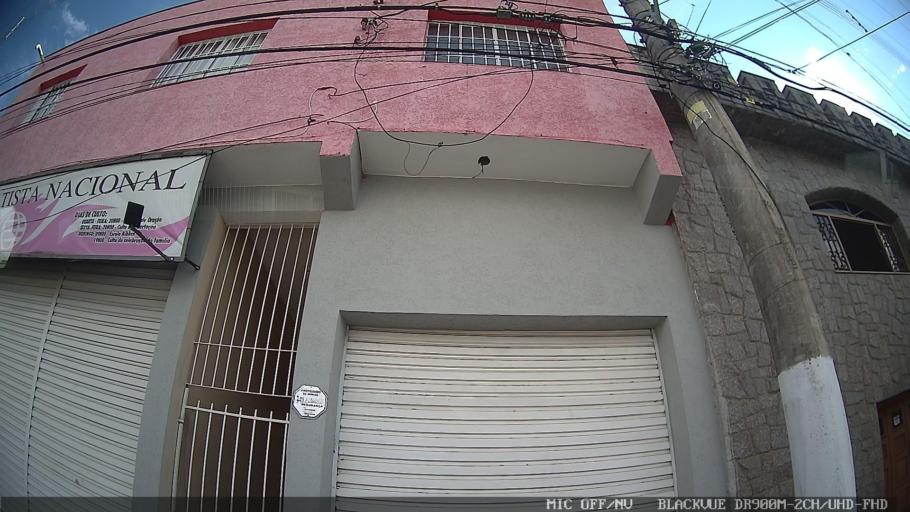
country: BR
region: Sao Paulo
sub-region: Braganca Paulista
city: Braganca Paulista
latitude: -22.9557
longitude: -46.5344
